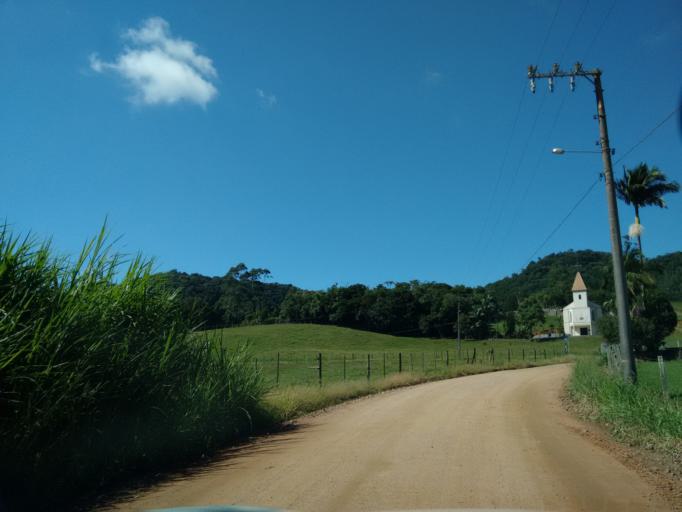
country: BR
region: Santa Catarina
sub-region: Pomerode
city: Pomerode
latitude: -26.7665
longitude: -49.1813
